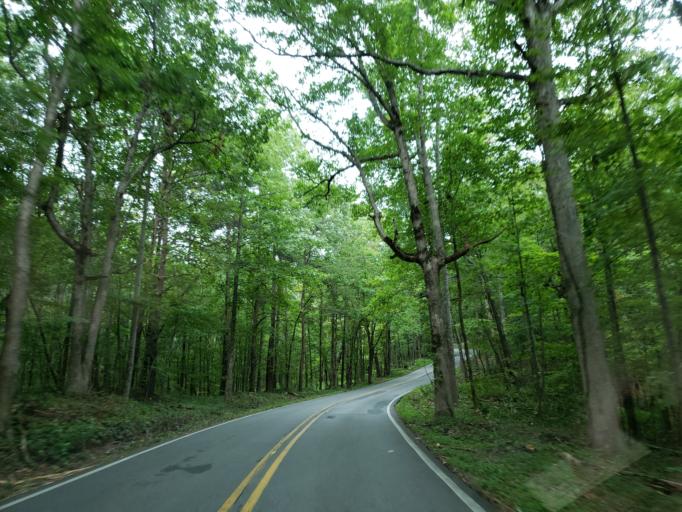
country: US
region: Georgia
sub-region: Pickens County
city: Jasper
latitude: 34.4115
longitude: -84.5296
